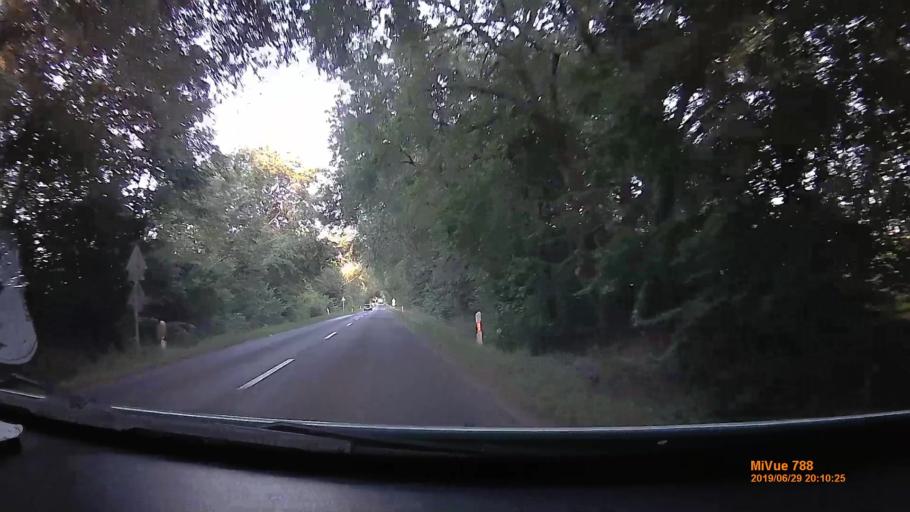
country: HU
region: Pest
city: Telki
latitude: 47.5353
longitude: 18.7755
